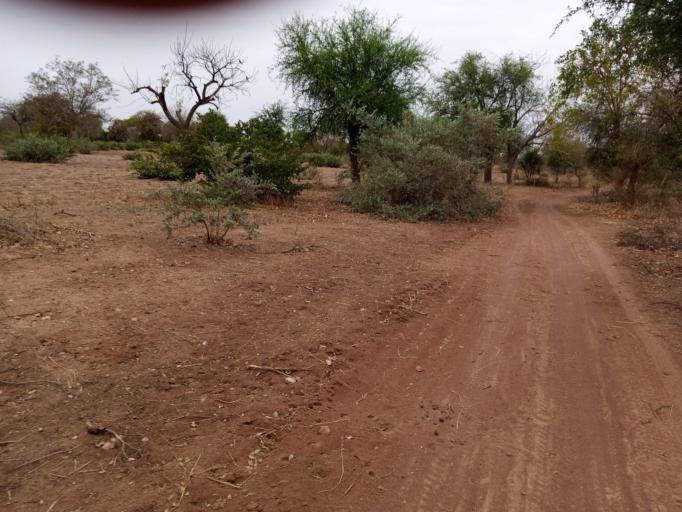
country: BF
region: Boucle du Mouhoun
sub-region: Province de la Kossi
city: Nouna
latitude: 12.8355
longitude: -4.0773
